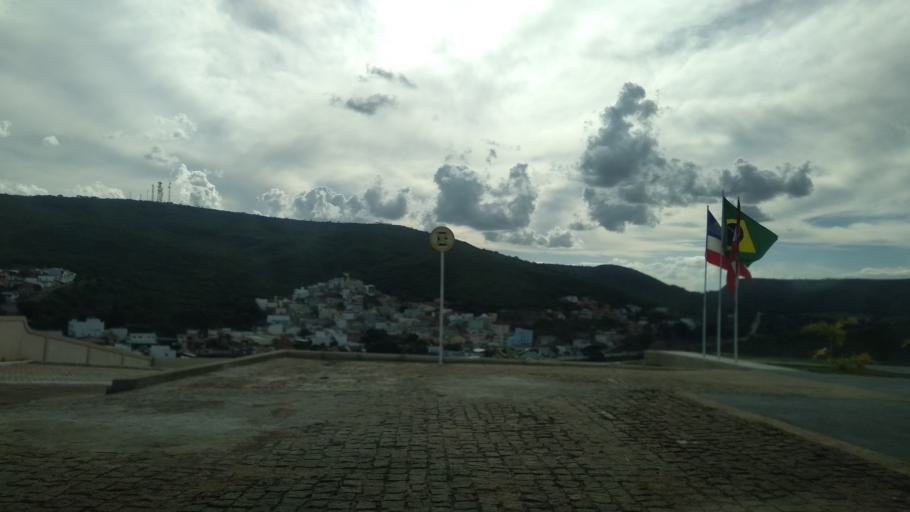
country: BR
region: Bahia
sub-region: Caetite
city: Caetite
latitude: -14.0618
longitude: -42.4934
